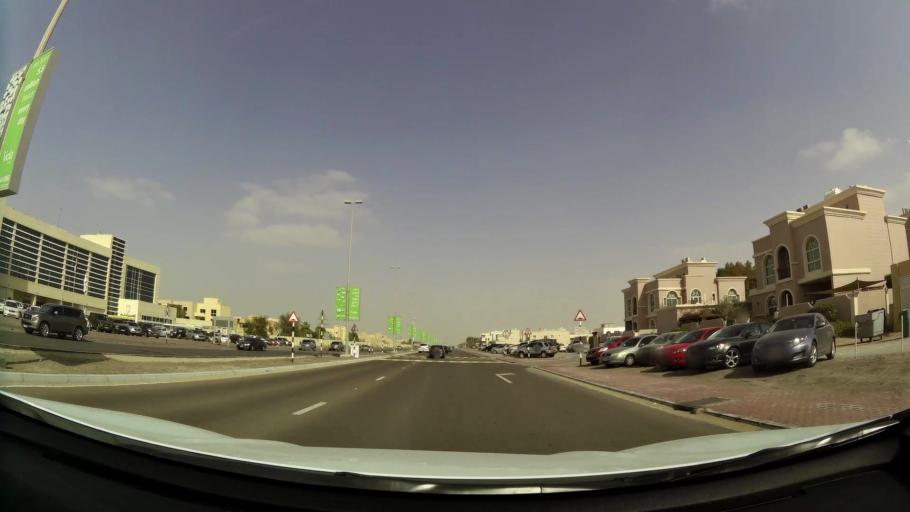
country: AE
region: Abu Dhabi
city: Abu Dhabi
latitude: 24.4249
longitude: 54.5470
